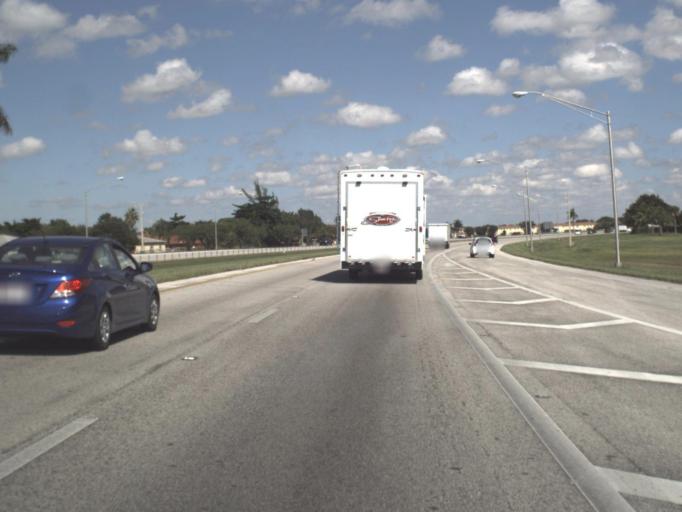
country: US
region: Florida
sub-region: Miami-Dade County
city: Leisure City
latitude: 25.5035
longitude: -80.4170
